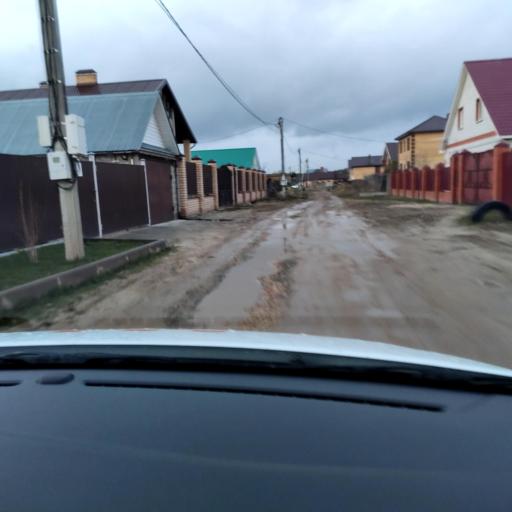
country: RU
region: Tatarstan
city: Stolbishchi
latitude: 55.6928
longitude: 49.1542
